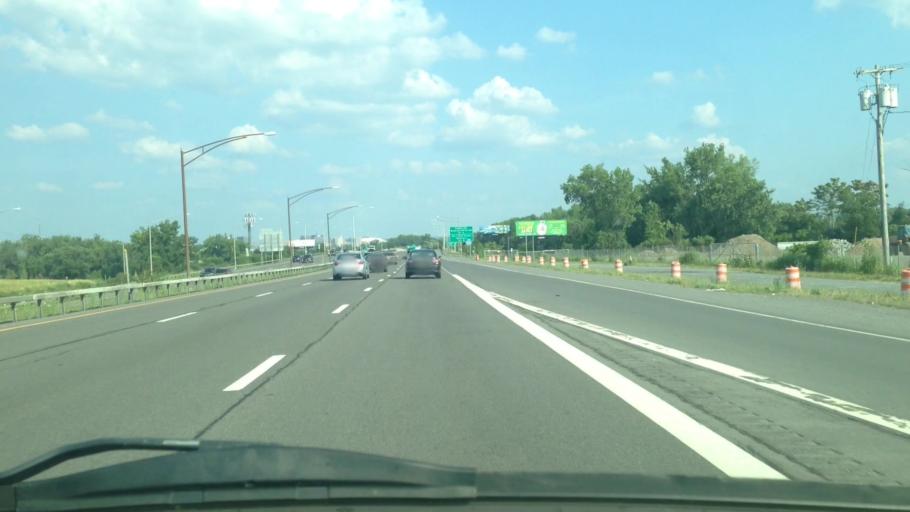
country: US
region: New York
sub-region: Onondaga County
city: Solvay
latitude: 43.0631
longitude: -76.1926
